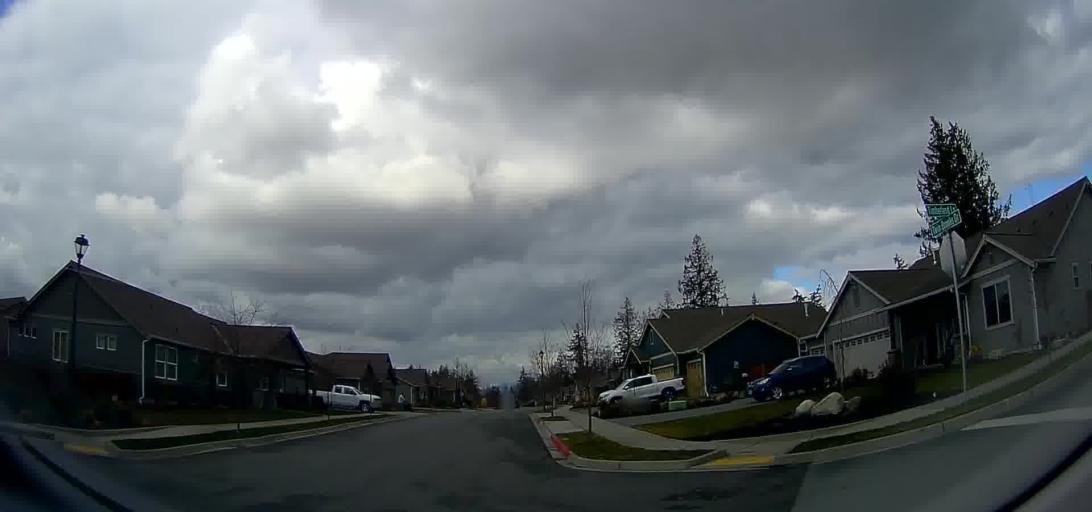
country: US
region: Washington
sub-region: Skagit County
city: Big Lake
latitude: 48.4244
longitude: -122.2813
